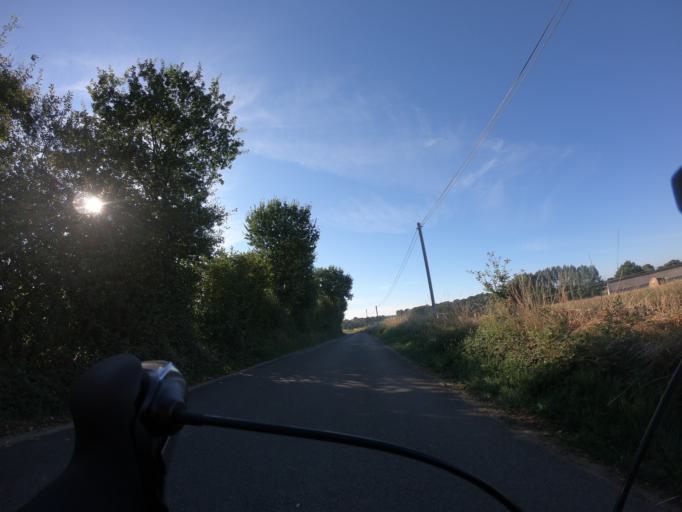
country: FR
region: Pays de la Loire
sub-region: Departement de la Mayenne
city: Pre-en-Pail
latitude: 48.5451
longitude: -0.2288
